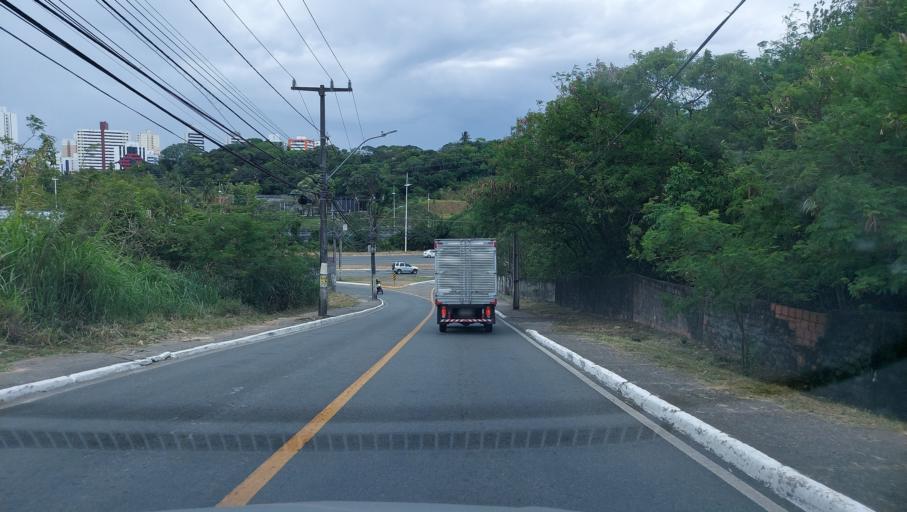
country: BR
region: Bahia
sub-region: Salvador
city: Salvador
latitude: -12.9687
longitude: -38.4435
